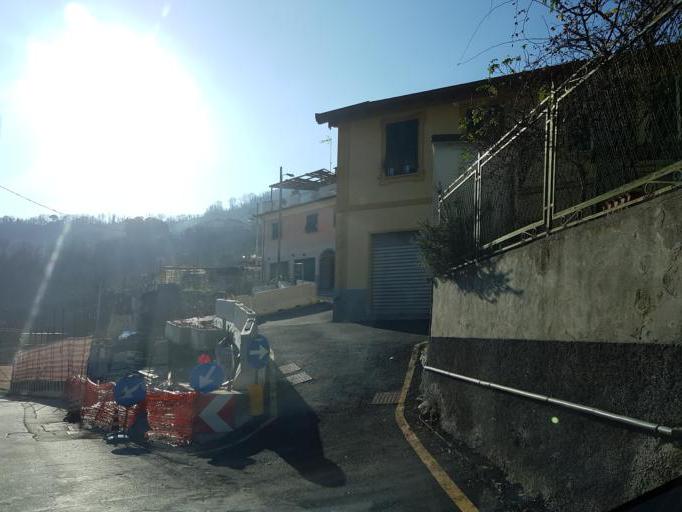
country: IT
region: Liguria
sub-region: Provincia di Genova
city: Campomorone
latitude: 44.5101
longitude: 8.8834
